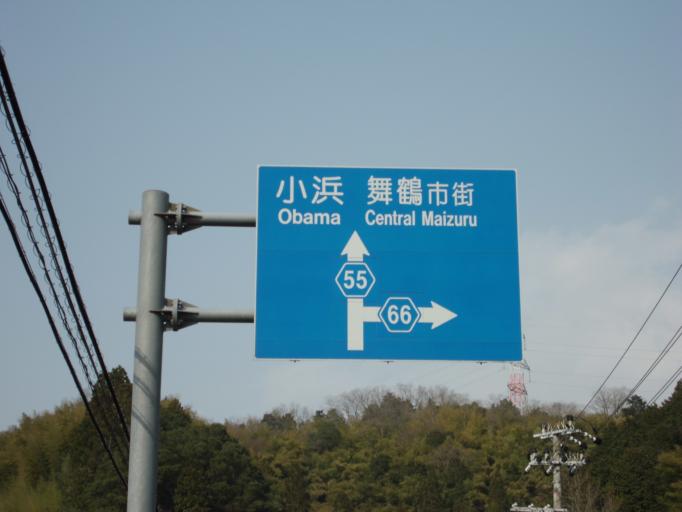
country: JP
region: Kyoto
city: Maizuru
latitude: 35.4327
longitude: 135.2598
